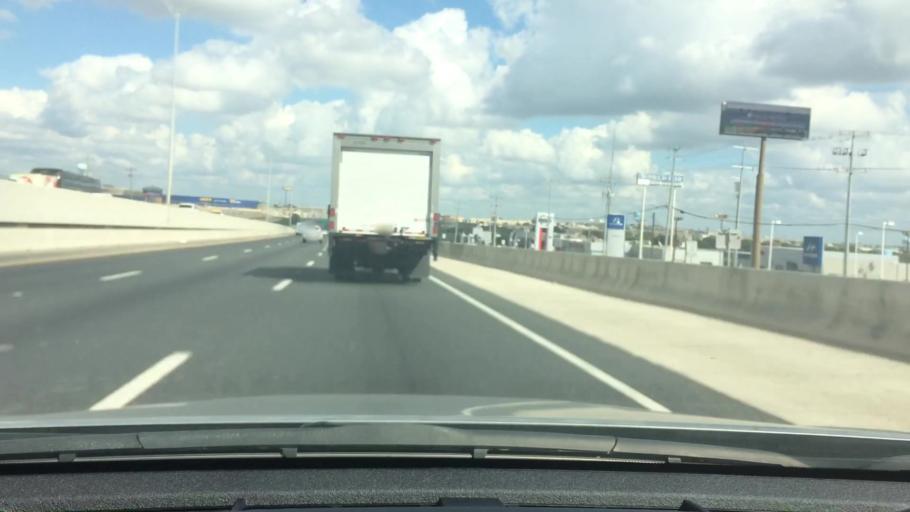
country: US
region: Texas
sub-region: Bexar County
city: Live Oak
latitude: 29.5564
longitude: -98.3464
